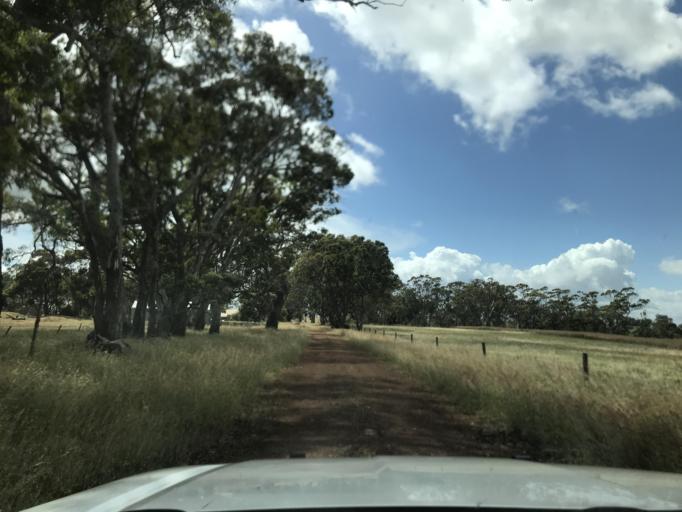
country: AU
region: South Australia
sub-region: Wattle Range
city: Penola
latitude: -37.1853
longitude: 141.4821
